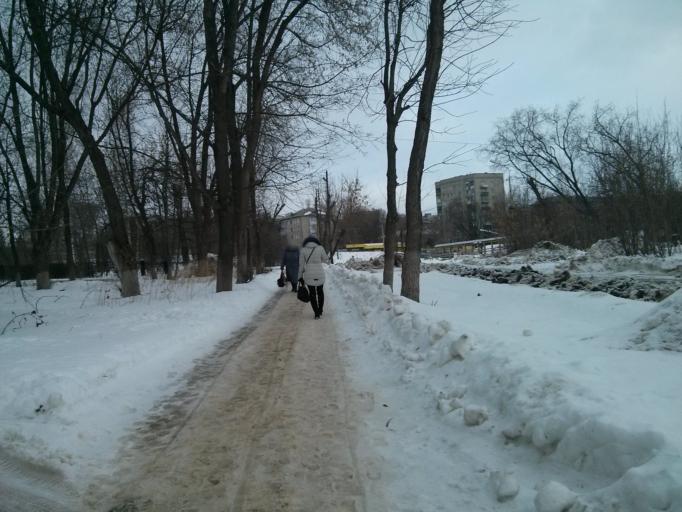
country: RU
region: Vladimir
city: Murom
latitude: 55.5627
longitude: 42.0573
